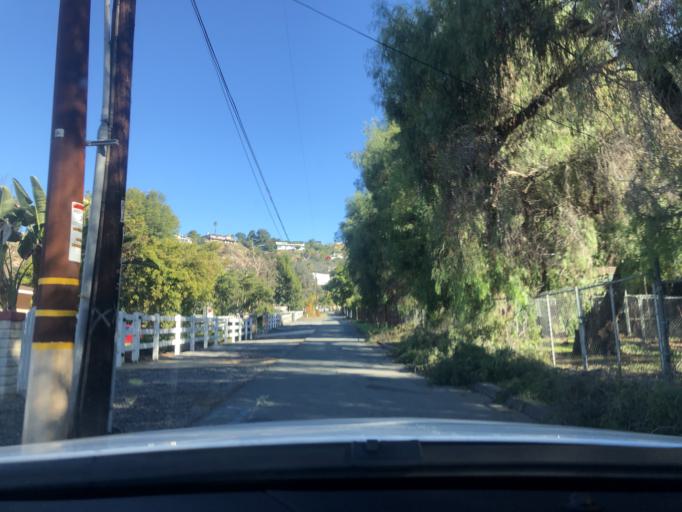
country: US
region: California
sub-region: San Diego County
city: El Cajon
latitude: 32.7784
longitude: -116.9424
